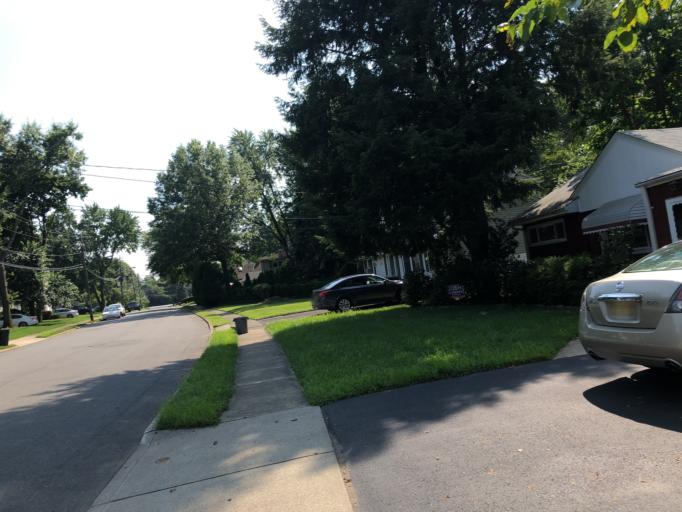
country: US
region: New Jersey
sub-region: Bergen County
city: Fair Lawn
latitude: 40.9456
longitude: -74.1100
